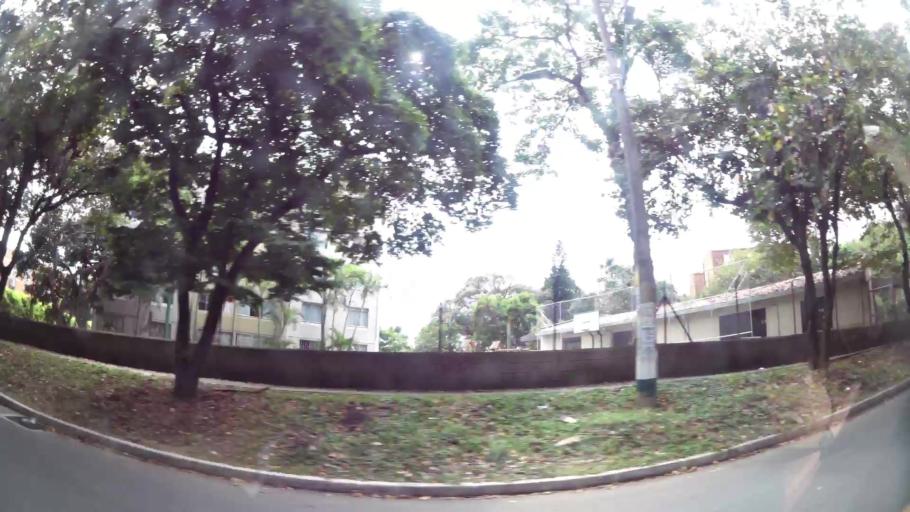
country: CO
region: Antioquia
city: Itagui
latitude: 6.1925
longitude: -75.5964
